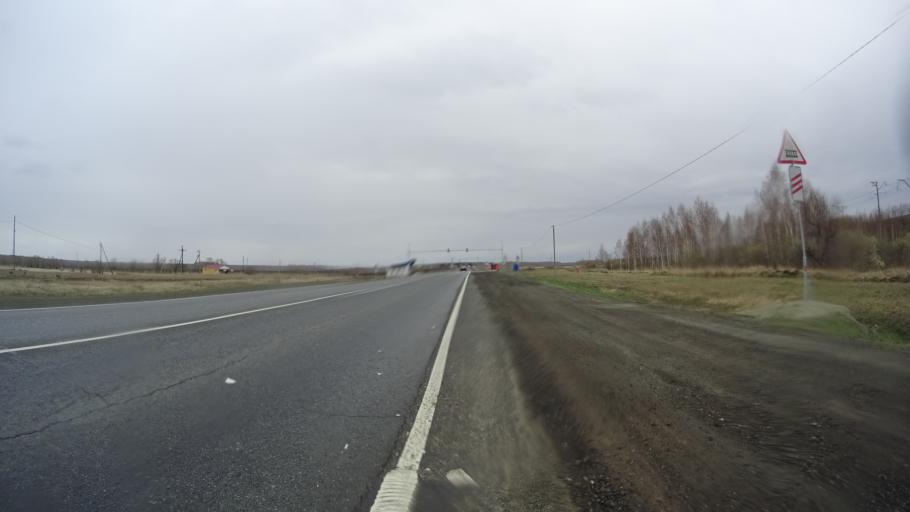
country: RU
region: Chelyabinsk
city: Krasnogorskiy
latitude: 54.6234
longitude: 61.2810
